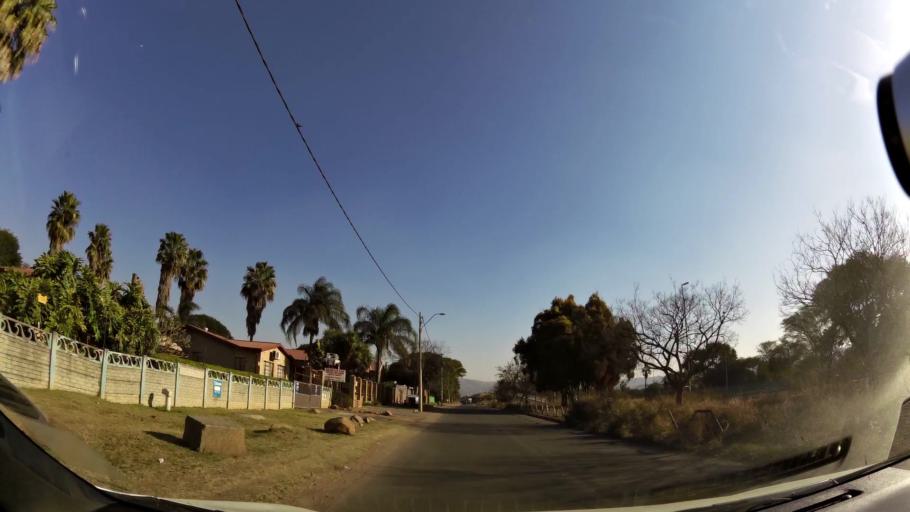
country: ZA
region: North-West
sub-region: Bojanala Platinum District Municipality
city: Rustenburg
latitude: -25.6536
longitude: 27.2473
